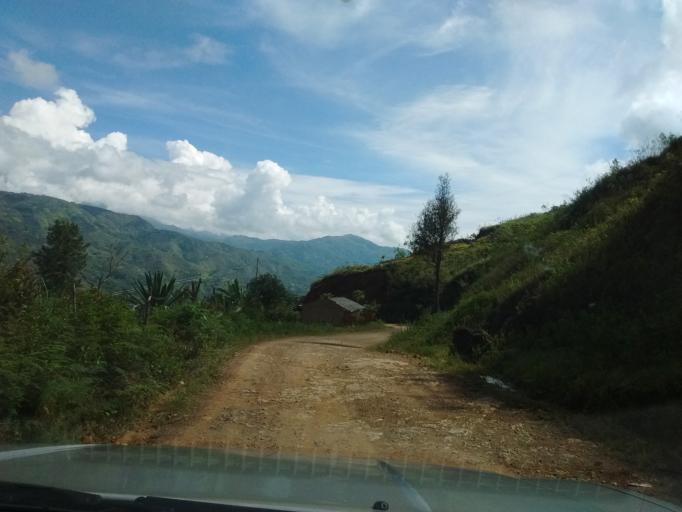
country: CO
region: Cauca
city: Morales
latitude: 2.6908
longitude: -76.7471
